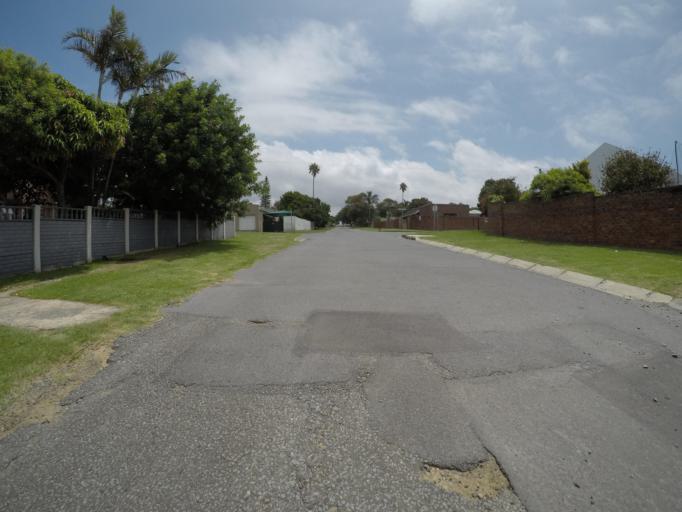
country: ZA
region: Eastern Cape
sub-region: Buffalo City Metropolitan Municipality
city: East London
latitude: -32.9440
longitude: 28.0181
